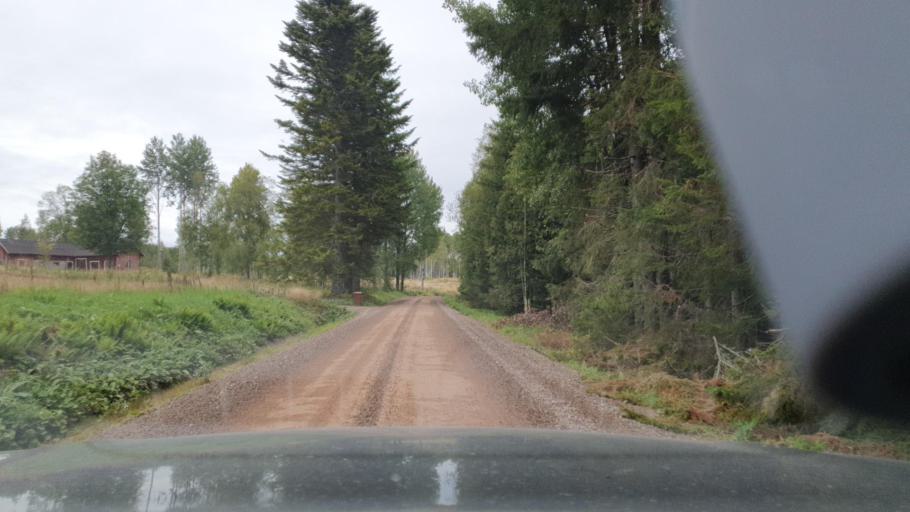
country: SE
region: Vaermland
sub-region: Arvika Kommun
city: Arvika
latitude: 59.9705
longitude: 12.6594
